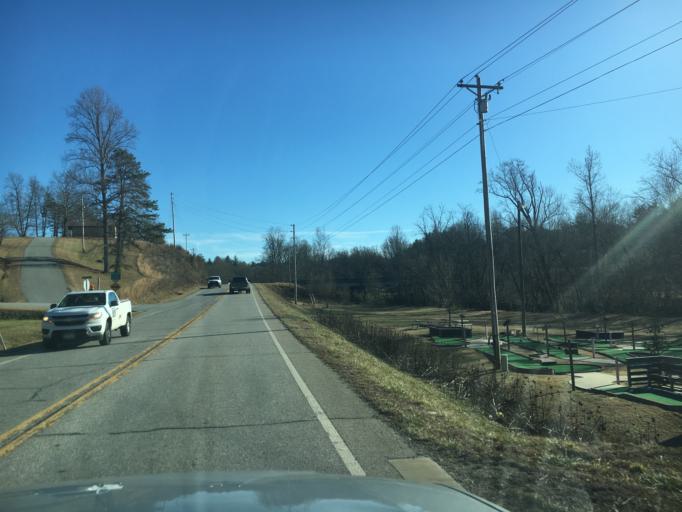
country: US
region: Georgia
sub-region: Union County
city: Blairsville
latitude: 34.8219
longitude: -83.9044
